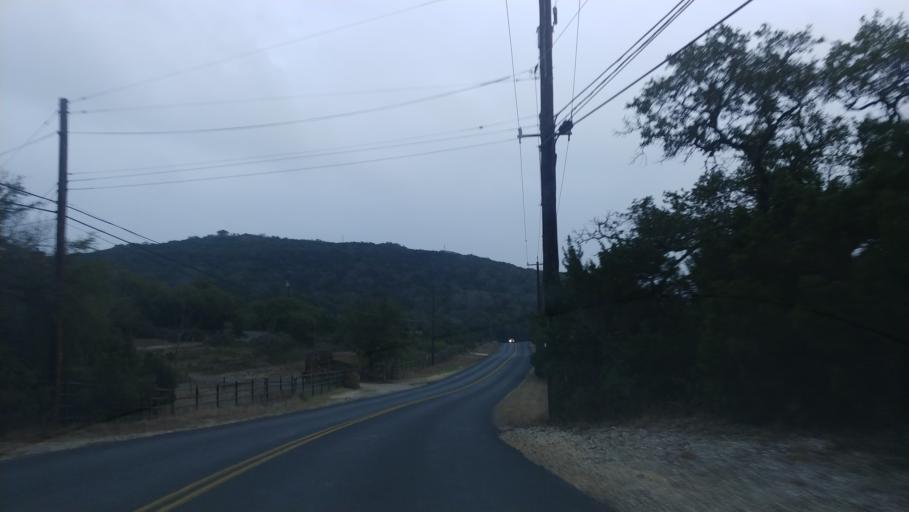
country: US
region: Texas
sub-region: Bexar County
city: Cross Mountain
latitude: 29.6377
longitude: -98.6782
